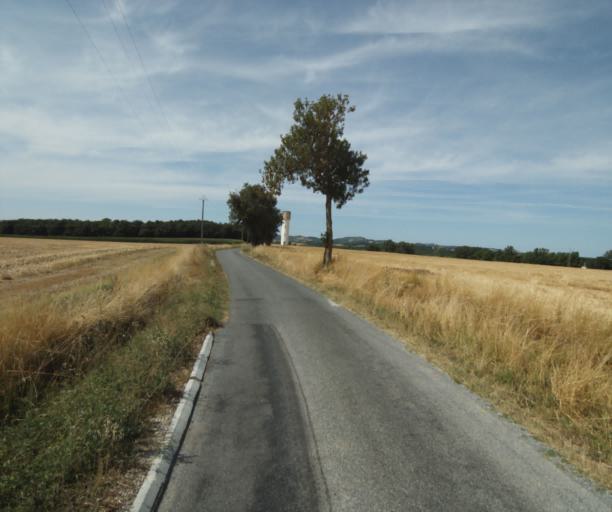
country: FR
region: Midi-Pyrenees
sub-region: Departement du Tarn
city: Soreze
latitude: 43.5031
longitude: 2.0472
